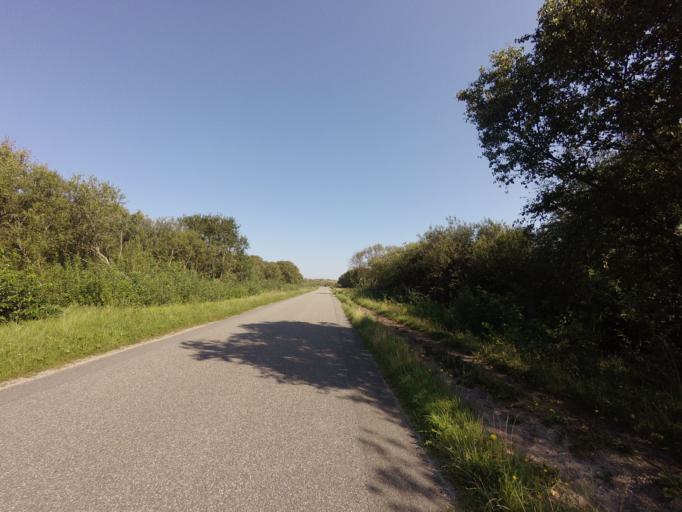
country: NL
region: Friesland
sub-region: Gemeente Schiermonnikoog
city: Schiermonnikoog
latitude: 53.4943
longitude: 6.1853
